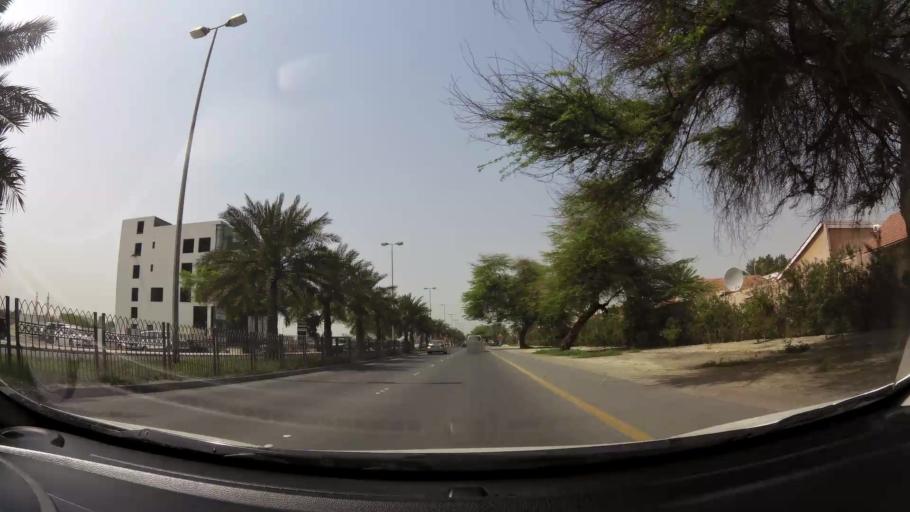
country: BH
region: Manama
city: Jidd Hafs
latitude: 26.2178
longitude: 50.4825
